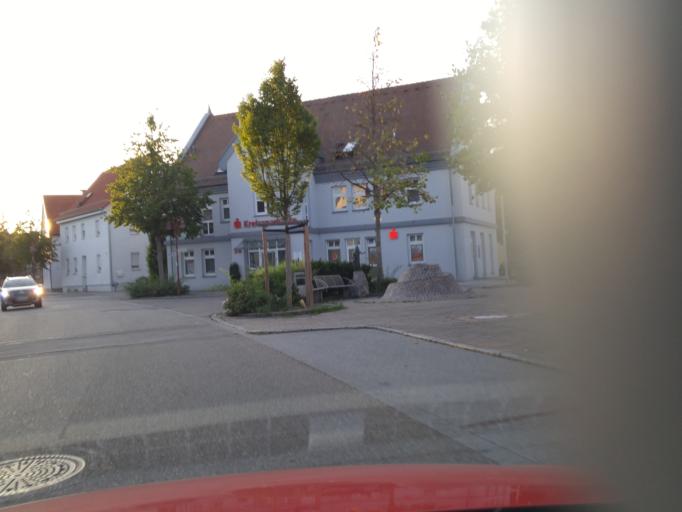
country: DE
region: Baden-Wuerttemberg
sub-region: Regierungsbezirk Stuttgart
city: Untereisesheim
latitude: 49.1967
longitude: 9.1984
